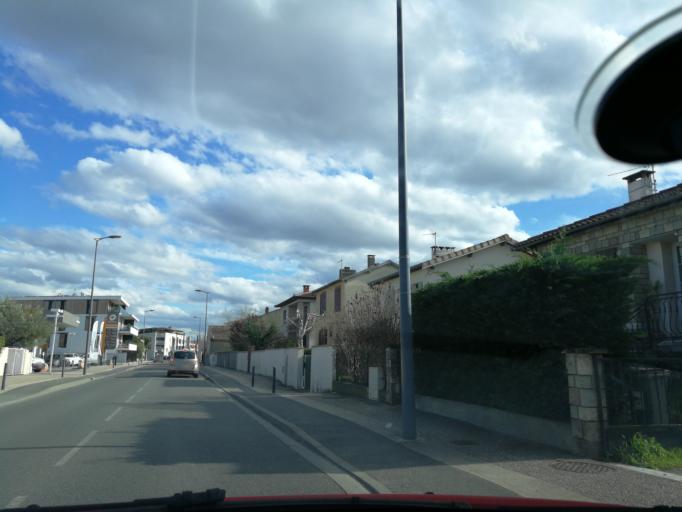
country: FR
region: Midi-Pyrenees
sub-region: Departement de la Haute-Garonne
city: Blagnac
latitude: 43.6387
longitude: 1.3897
